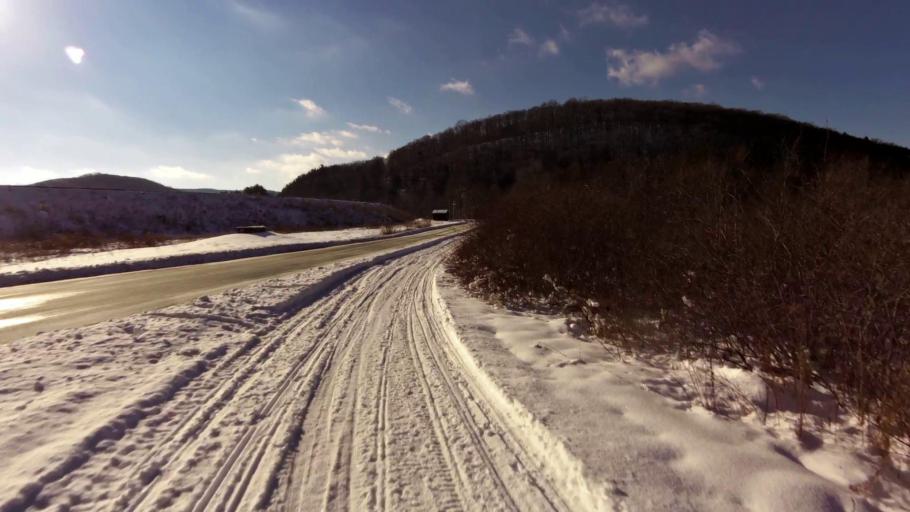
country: US
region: New York
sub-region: Cattaraugus County
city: Salamanca
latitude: 42.1073
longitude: -78.7483
